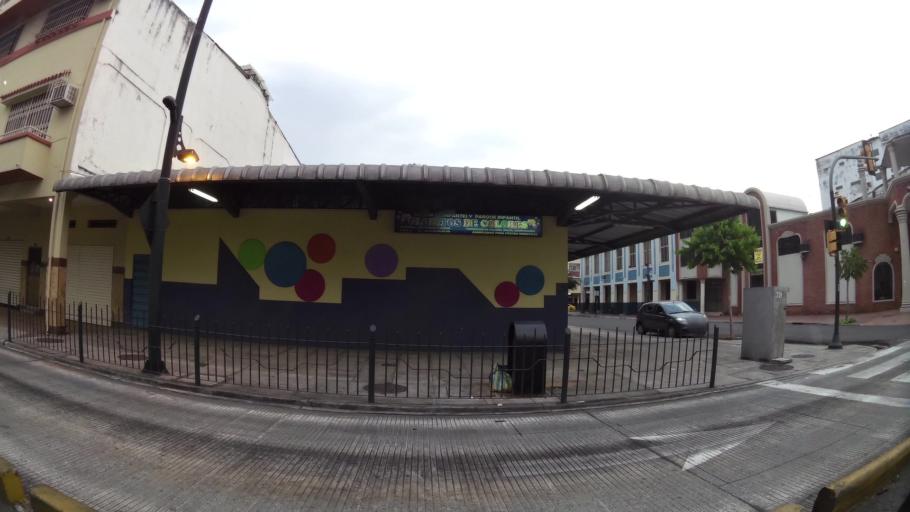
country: EC
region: Guayas
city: Guayaquil
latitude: -2.2123
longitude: -79.8868
